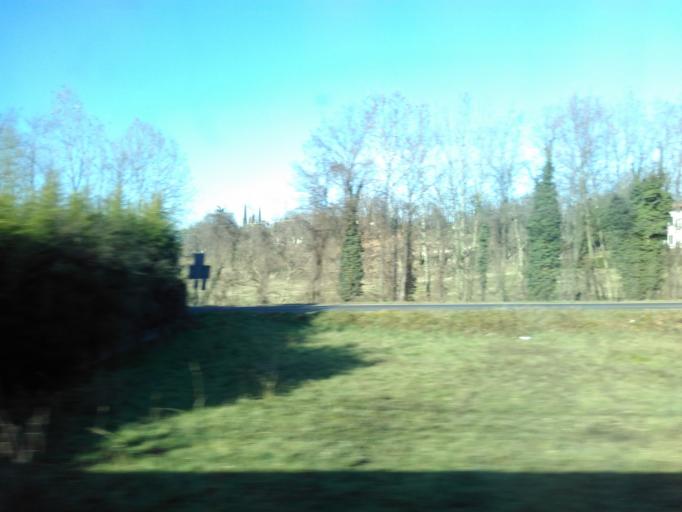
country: IT
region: Lombardy
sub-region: Provincia di Brescia
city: Lonato
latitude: 45.4644
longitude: 10.5056
